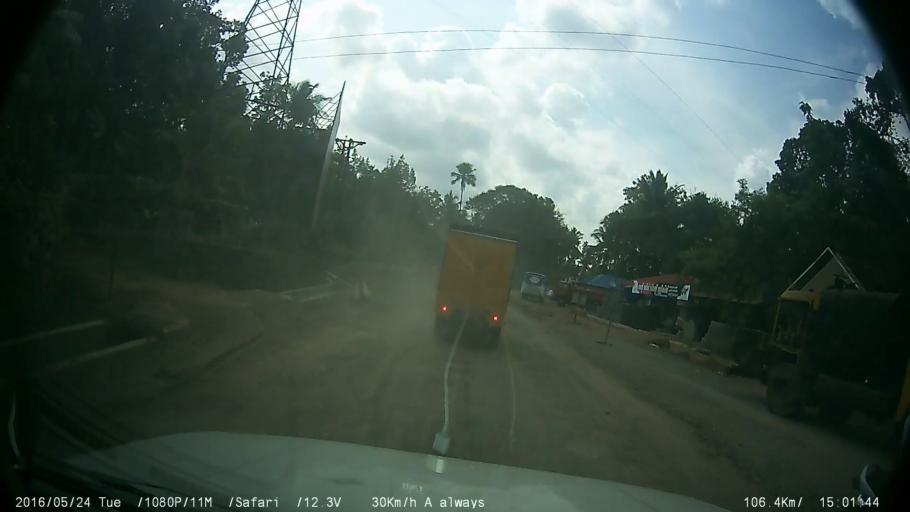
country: IN
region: Kerala
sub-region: Ernakulam
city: Piravam
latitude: 9.8405
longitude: 76.5920
